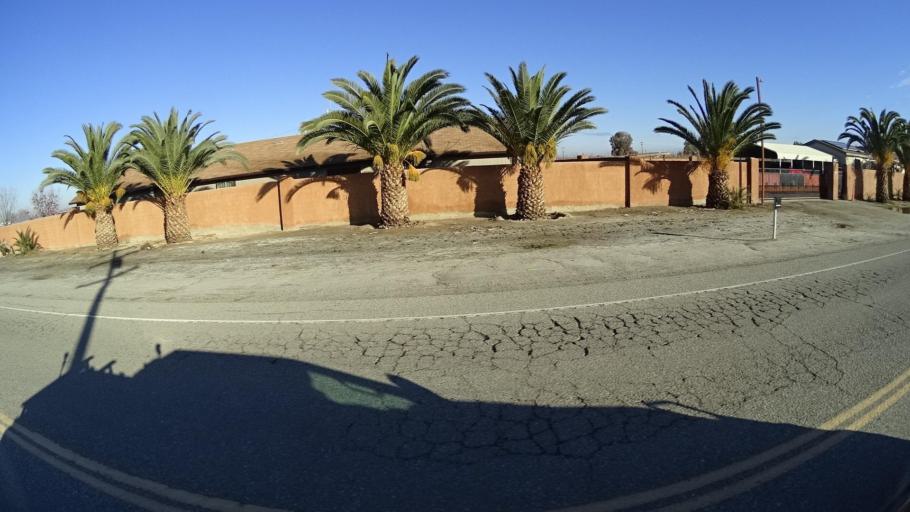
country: US
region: California
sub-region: Kern County
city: Delano
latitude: 35.7757
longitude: -119.3399
